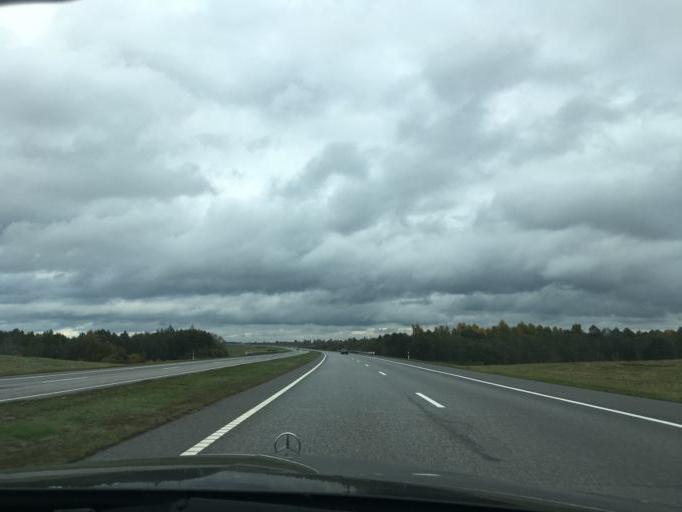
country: BY
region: Vitebsk
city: Kokhanava
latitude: 54.4733
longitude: 29.8836
